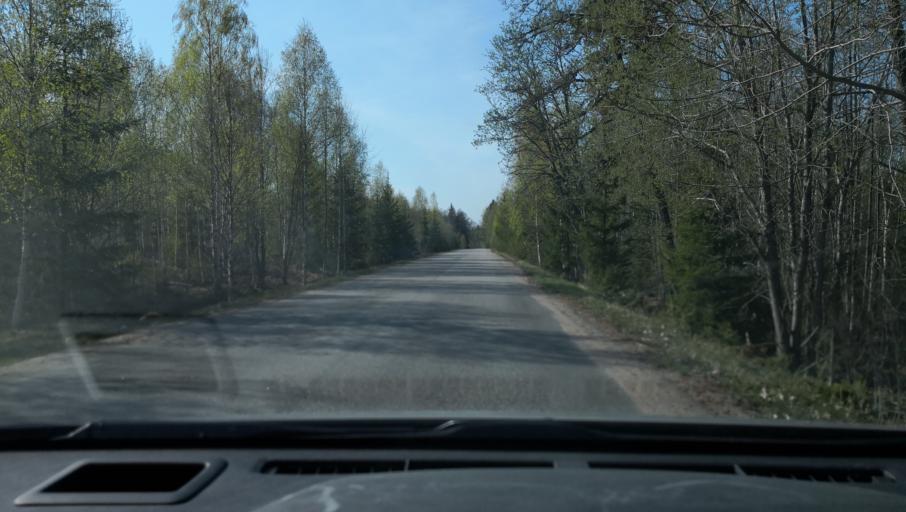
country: SE
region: Uppsala
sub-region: Heby Kommun
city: Tarnsjo
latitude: 60.2623
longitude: 16.9332
